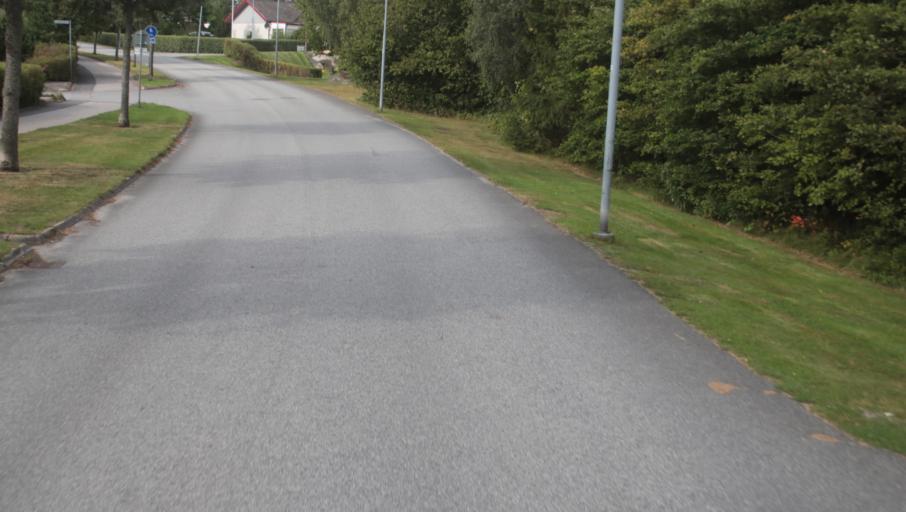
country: SE
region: Blekinge
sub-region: Karlshamns Kommun
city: Karlshamn
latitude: 56.2049
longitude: 14.8616
